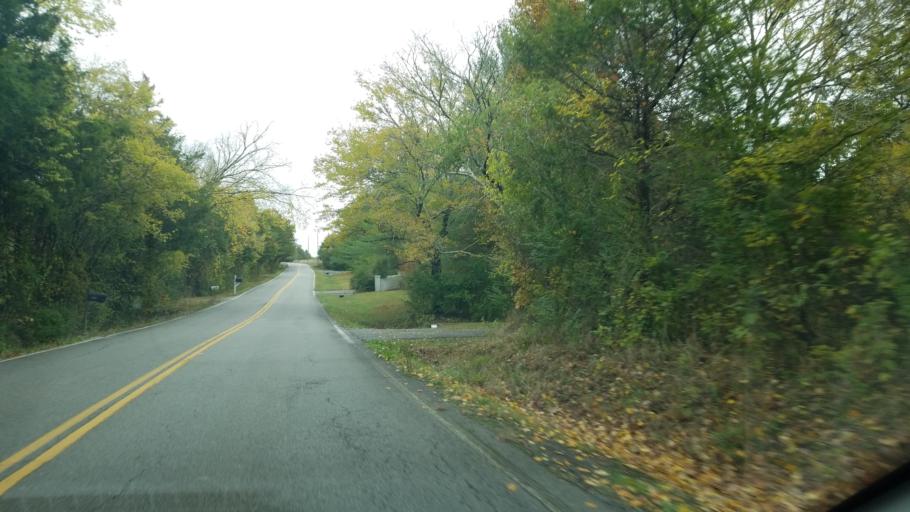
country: US
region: Tennessee
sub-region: Bradley County
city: Hopewell
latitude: 35.2509
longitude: -84.9818
